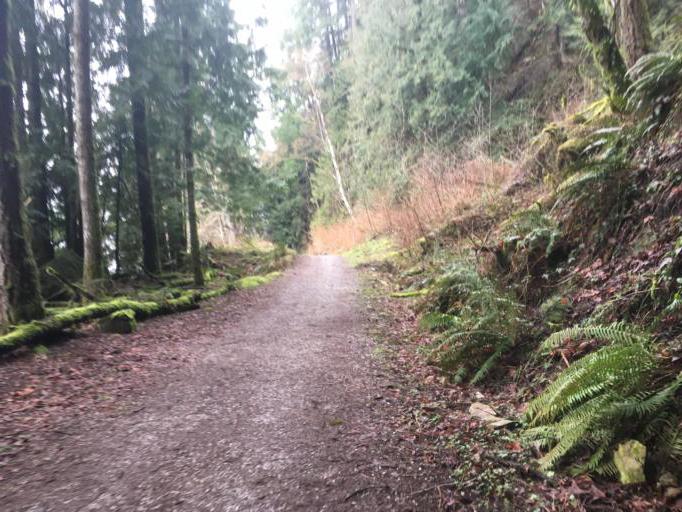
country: US
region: Washington
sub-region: Whatcom County
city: Sudden Valley
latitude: 48.7102
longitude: -122.2990
